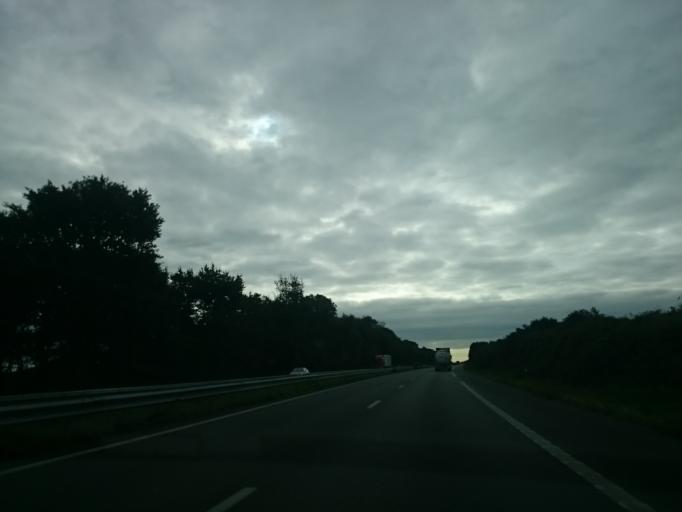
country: FR
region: Brittany
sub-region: Departement du Morbihan
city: Landaul
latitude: 47.7172
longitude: -3.0608
